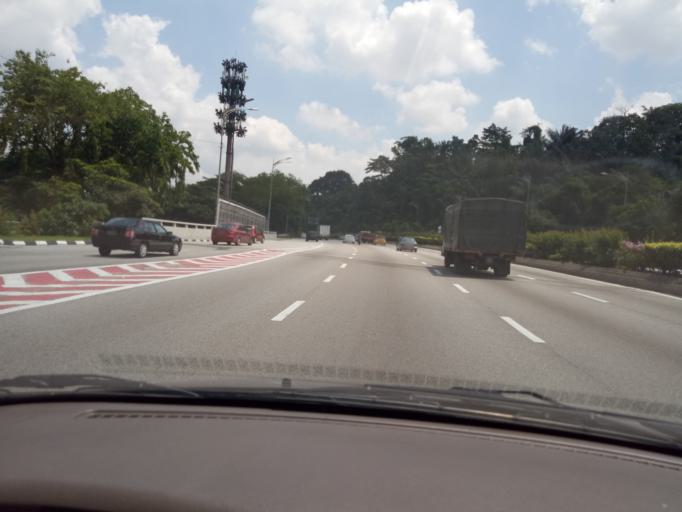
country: MY
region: Kuala Lumpur
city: Kuala Lumpur
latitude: 3.1375
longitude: 101.6905
